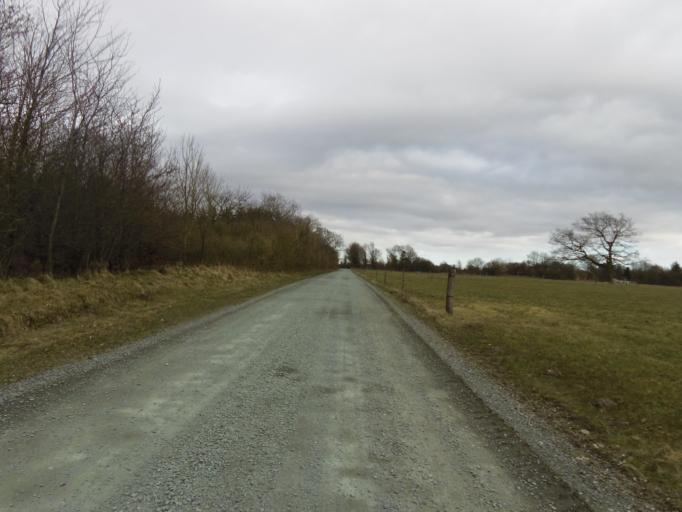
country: DK
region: South Denmark
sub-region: Tonder Kommune
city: Toftlund
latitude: 55.2119
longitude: 9.1702
